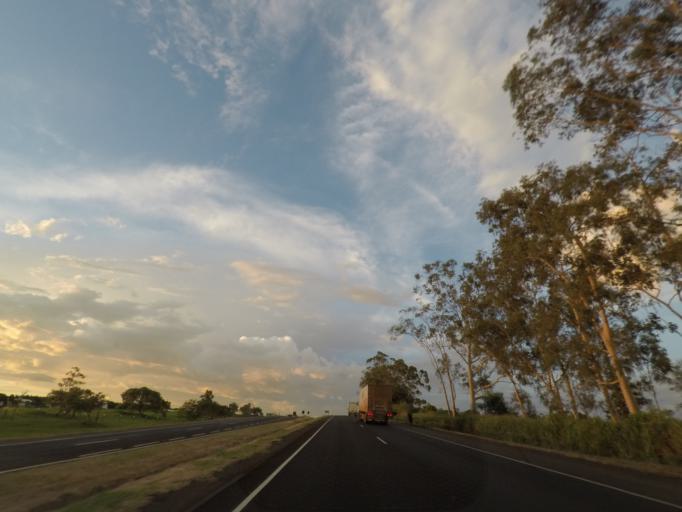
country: BR
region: Minas Gerais
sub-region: Uberaba
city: Uberaba
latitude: -19.6733
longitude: -47.9972
